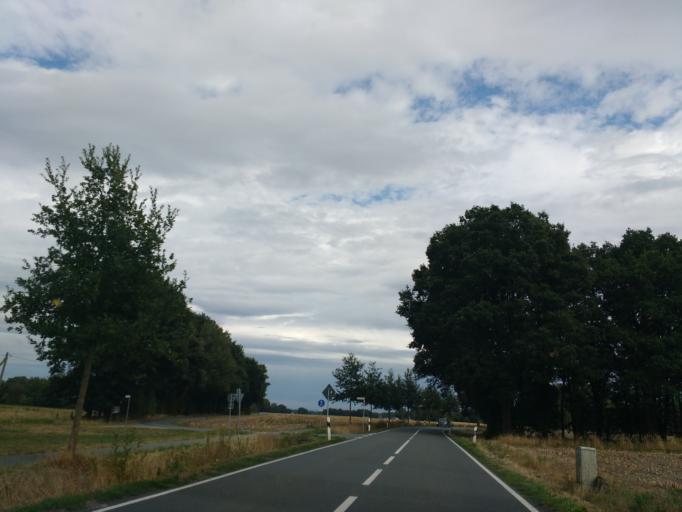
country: DE
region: North Rhine-Westphalia
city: Rietberg
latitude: 51.8254
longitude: 8.4581
